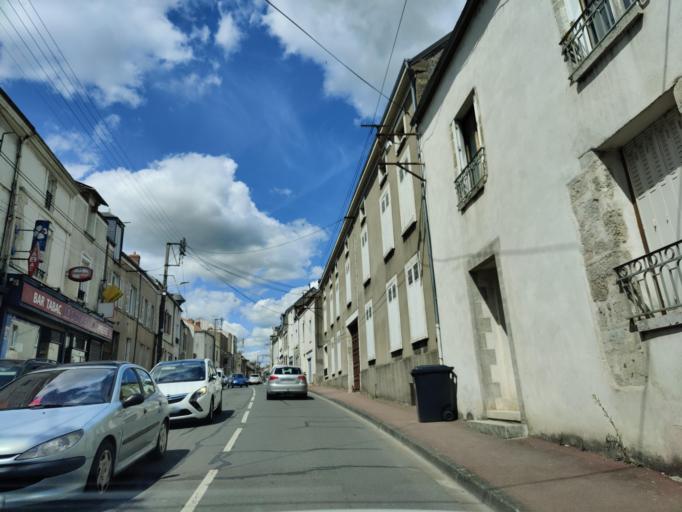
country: FR
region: Centre
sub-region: Departement du Loiret
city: Pithiviers
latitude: 48.1692
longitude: 2.2567
